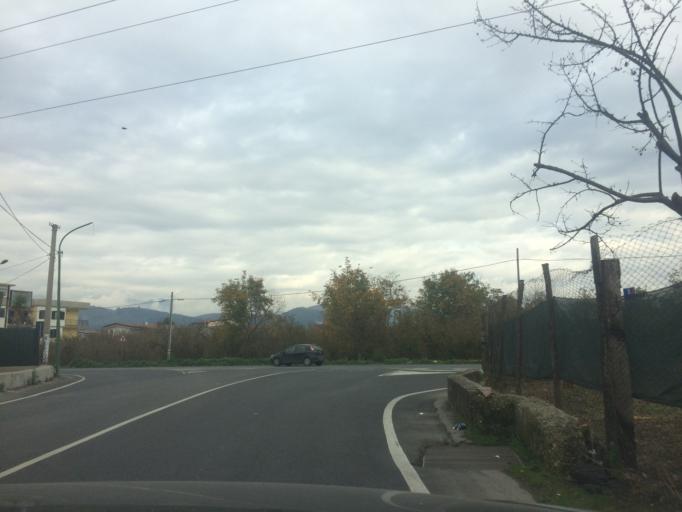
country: IT
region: Campania
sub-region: Provincia di Napoli
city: Piazzolla
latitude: 40.8979
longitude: 14.5234
